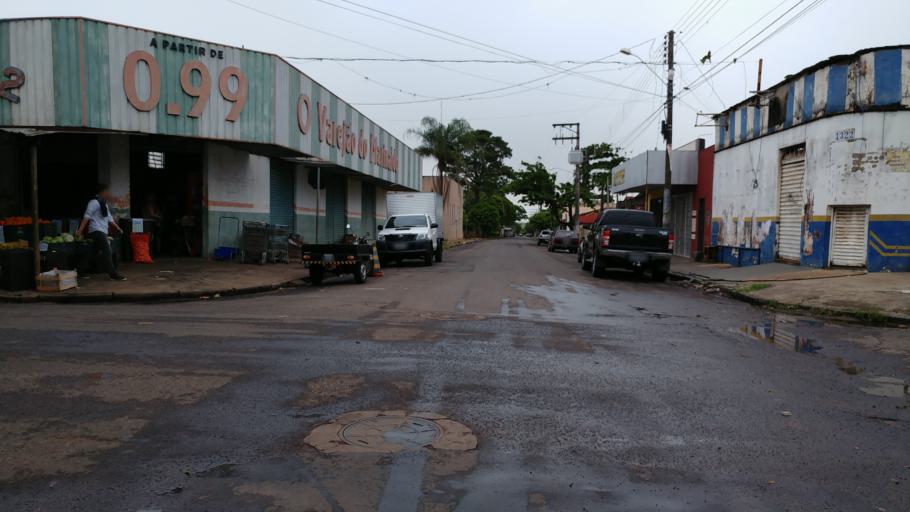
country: BR
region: Sao Paulo
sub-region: Paraguacu Paulista
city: Paraguacu Paulista
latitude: -22.4200
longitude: -50.5824
